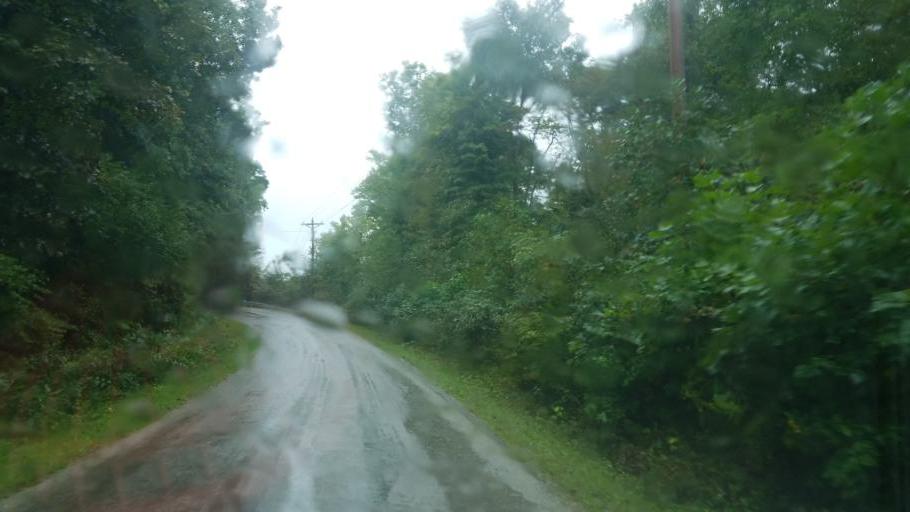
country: US
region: Kentucky
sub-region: Lewis County
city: Vanceburg
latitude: 38.7789
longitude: -83.2571
